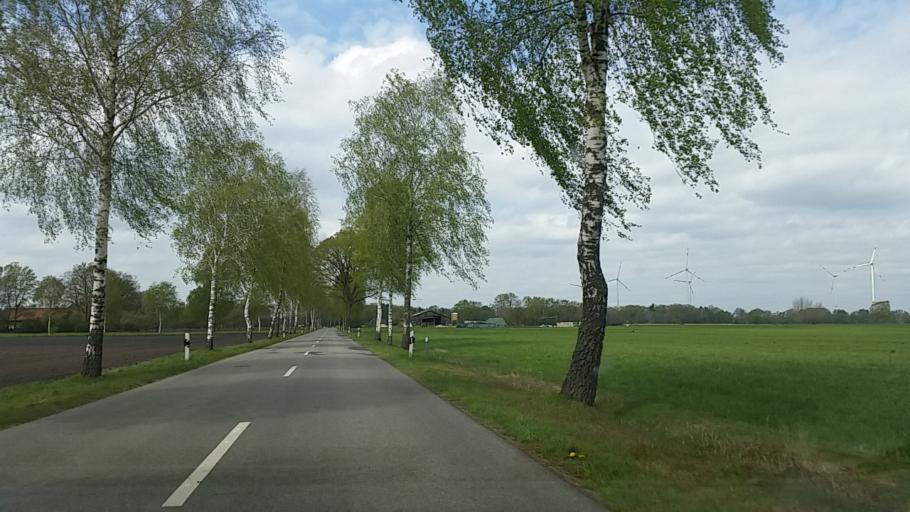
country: DE
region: Lower Saxony
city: Konigsmoor
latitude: 53.1963
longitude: 9.7171
